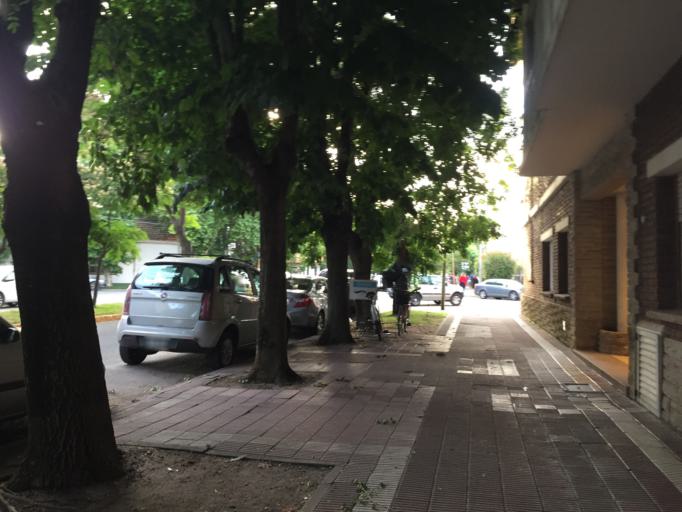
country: AR
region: Buenos Aires
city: Miramar
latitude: -38.2704
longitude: -57.8339
